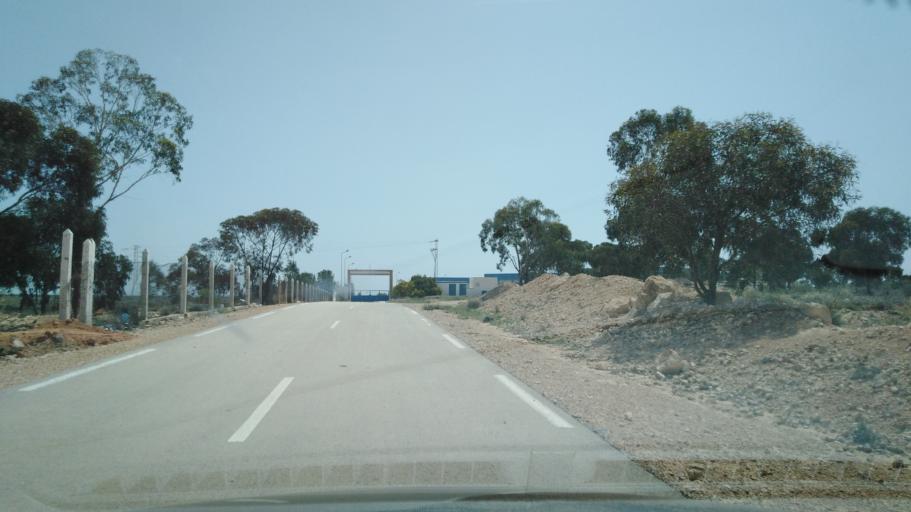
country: TN
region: Safaqis
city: Sfax
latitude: 34.7064
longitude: 10.5258
